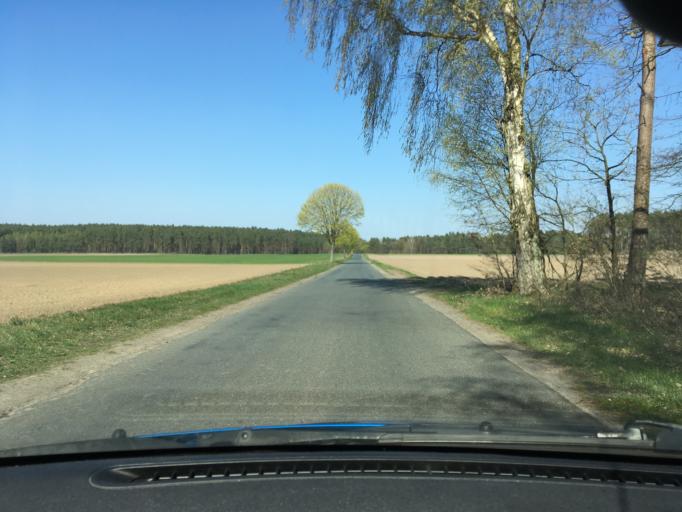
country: DE
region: Lower Saxony
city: Karwitz
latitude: 53.1188
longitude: 11.0056
